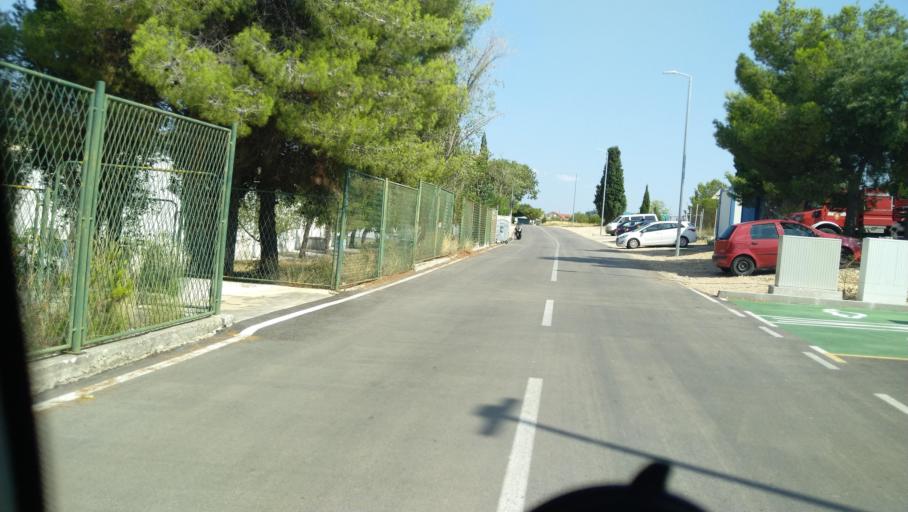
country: HR
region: Sibensko-Kniniska
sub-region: Grad Sibenik
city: Sibenik
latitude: 43.7166
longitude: 15.9082
